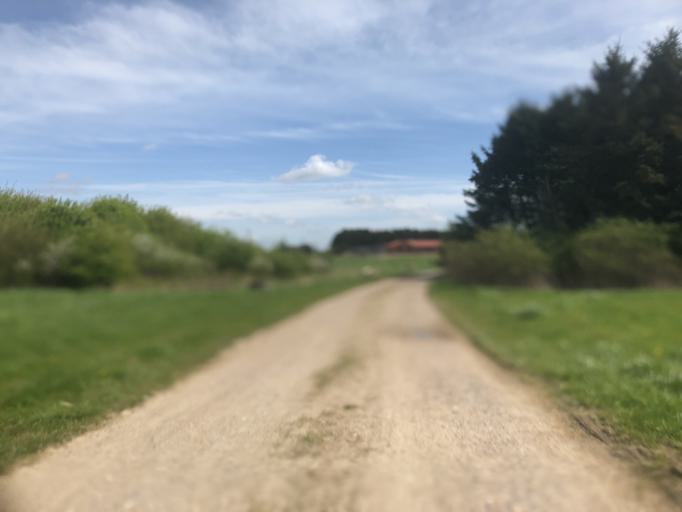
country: DK
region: Zealand
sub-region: Ringsted Kommune
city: Ringsted
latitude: 55.4527
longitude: 11.8011
